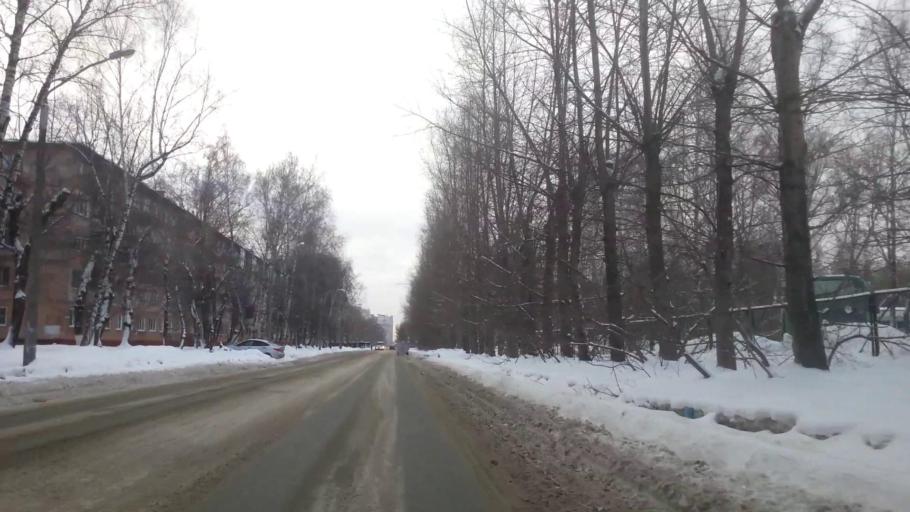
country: RU
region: Altai Krai
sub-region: Gorod Barnaulskiy
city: Barnaul
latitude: 53.3673
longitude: 83.6932
